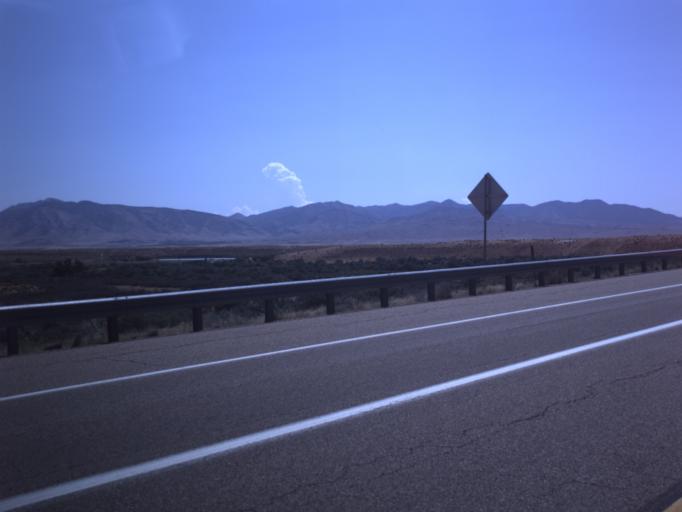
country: US
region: Utah
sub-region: Millard County
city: Delta
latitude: 39.3955
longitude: -112.5027
